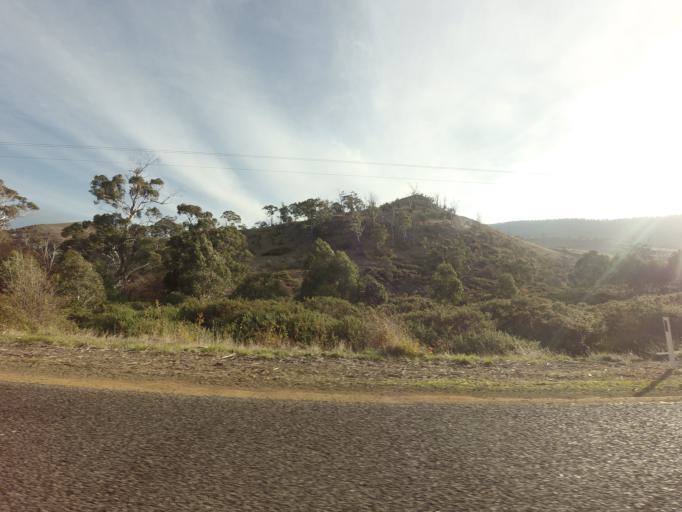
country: AU
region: Tasmania
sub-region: Brighton
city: Bridgewater
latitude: -42.4461
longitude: 147.1541
